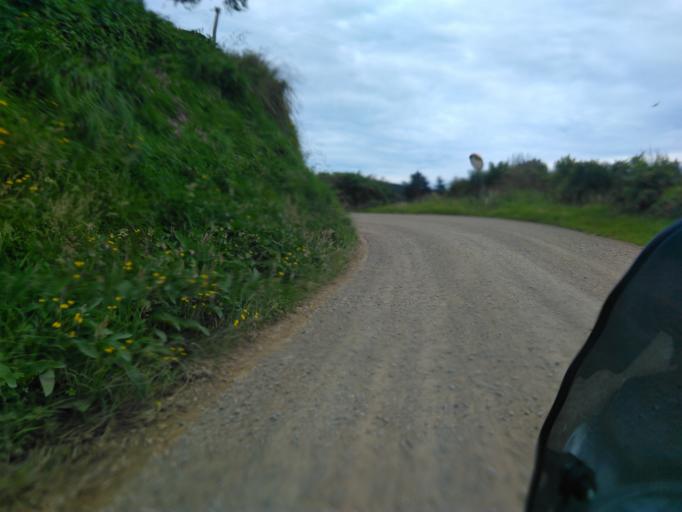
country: NZ
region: Bay of Plenty
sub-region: Opotiki District
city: Opotiki
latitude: -38.0134
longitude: 177.4216
